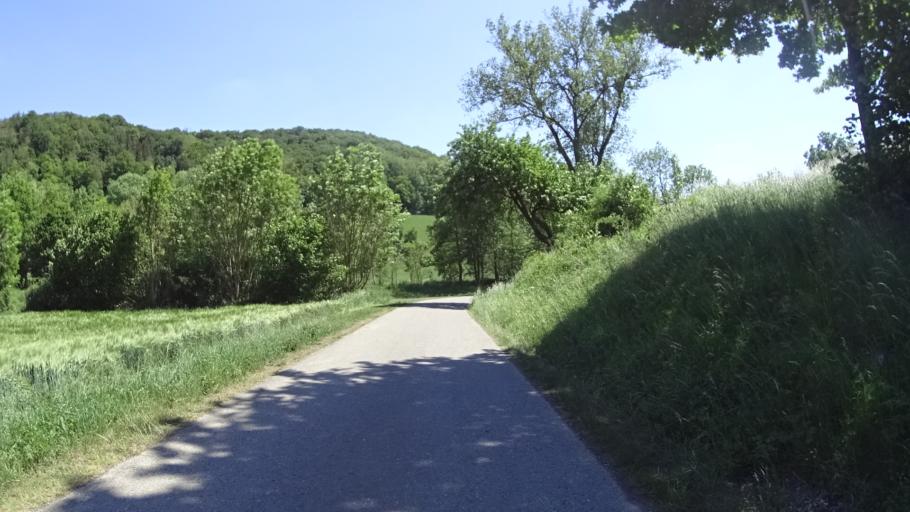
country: DE
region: Bavaria
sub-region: Regierungsbezirk Mittelfranken
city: Adelshofen
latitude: 49.4118
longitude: 10.1526
